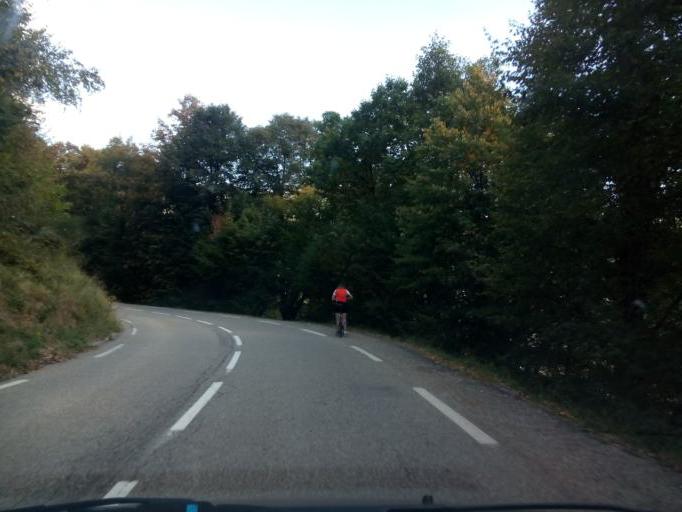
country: FR
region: Rhone-Alpes
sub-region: Departement de l'Isere
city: Vaulnaveys-le-Bas
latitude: 45.0449
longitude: 5.8251
